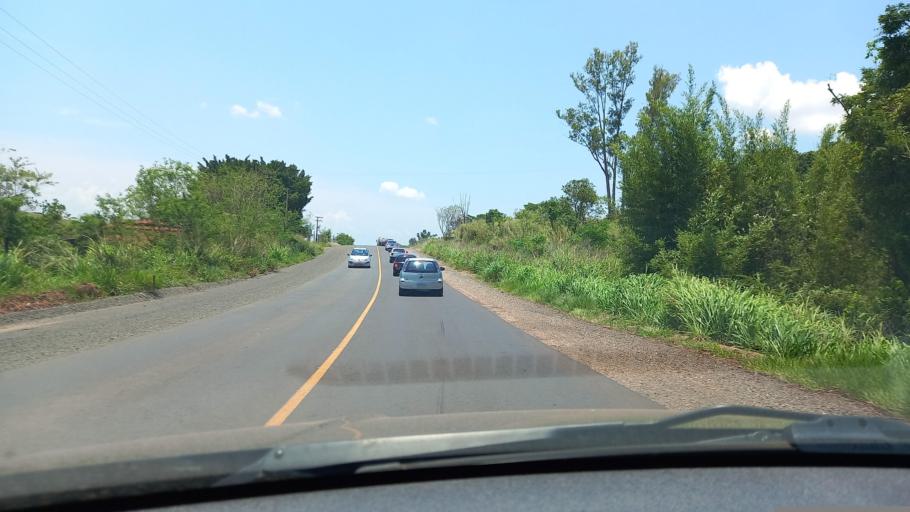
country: BR
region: Sao Paulo
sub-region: Moji-Guacu
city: Mogi-Gaucu
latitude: -22.3484
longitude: -46.8769
